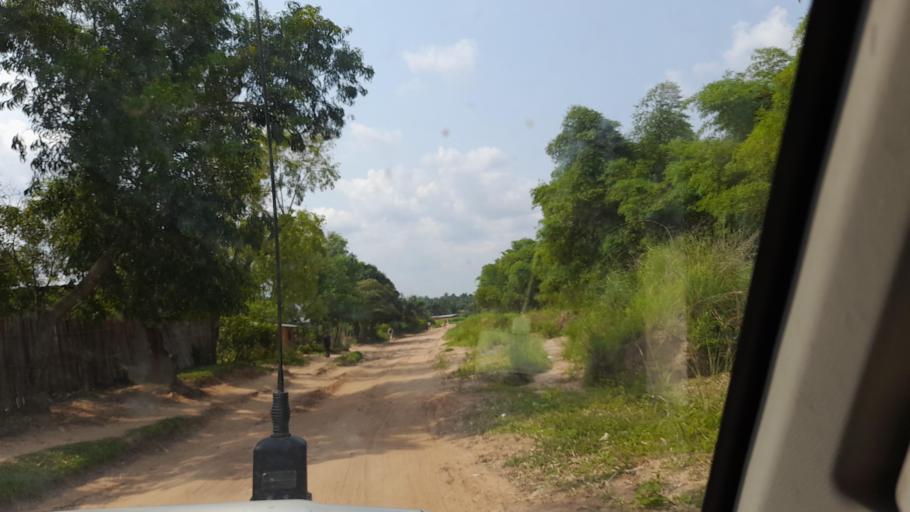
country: CD
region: Kasai-Occidental
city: Kananga
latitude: -5.9108
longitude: 22.4758
